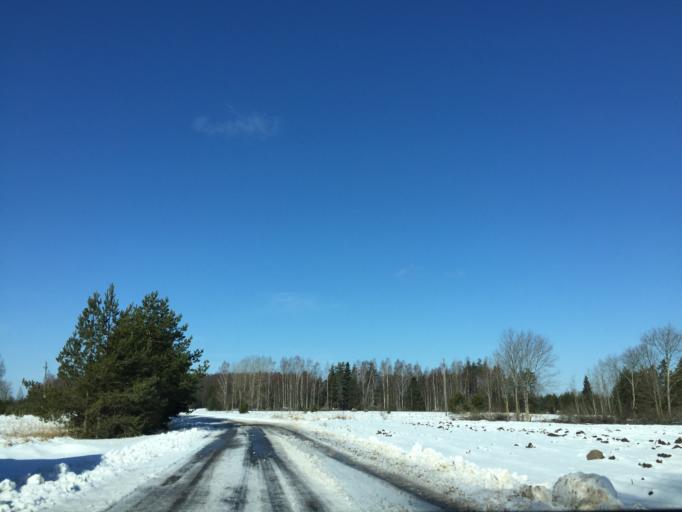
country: LV
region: Aloja
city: Staicele
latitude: 58.0260
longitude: 24.6023
